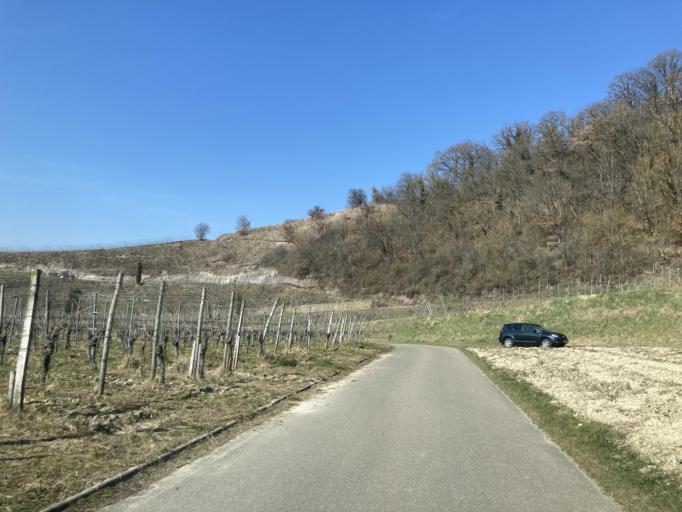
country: DE
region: Baden-Wuerttemberg
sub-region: Freiburg Region
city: Vogtsburg
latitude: 48.0726
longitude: 7.6392
